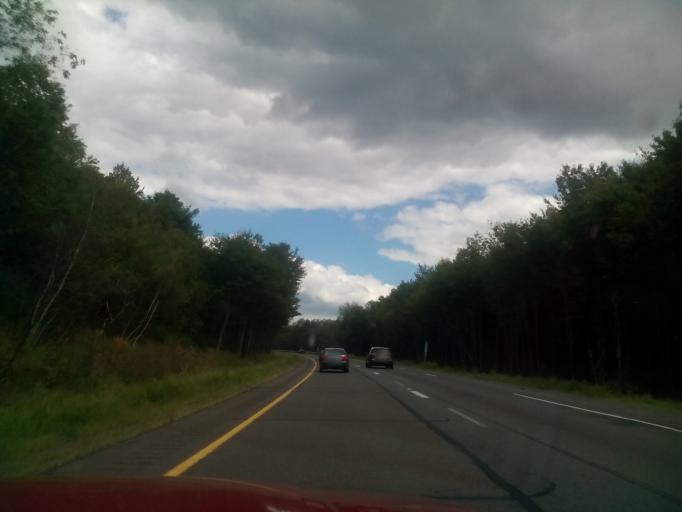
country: US
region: Pennsylvania
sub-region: Monroe County
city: Pocono Pines
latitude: 41.0724
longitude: -75.4943
